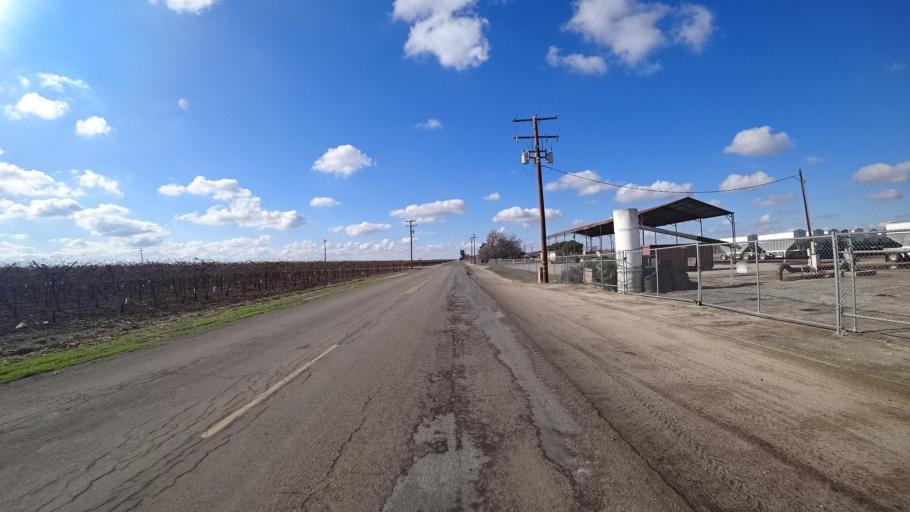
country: US
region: California
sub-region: Kern County
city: Delano
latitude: 35.7323
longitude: -119.2928
